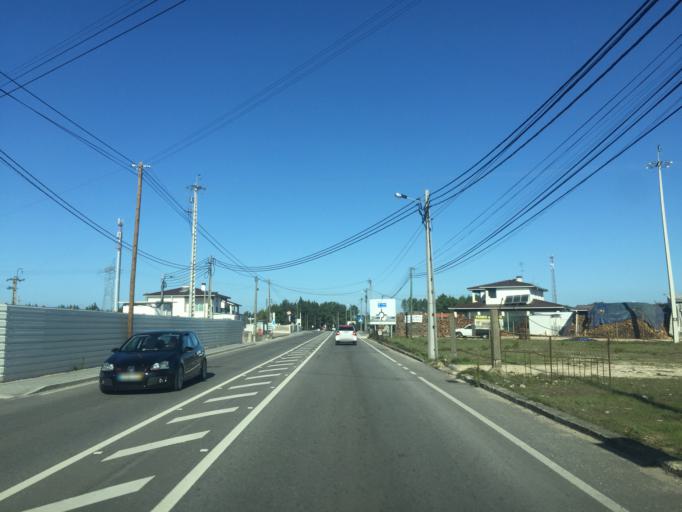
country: PT
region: Leiria
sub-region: Leiria
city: Amor
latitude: 39.7889
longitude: -8.8282
